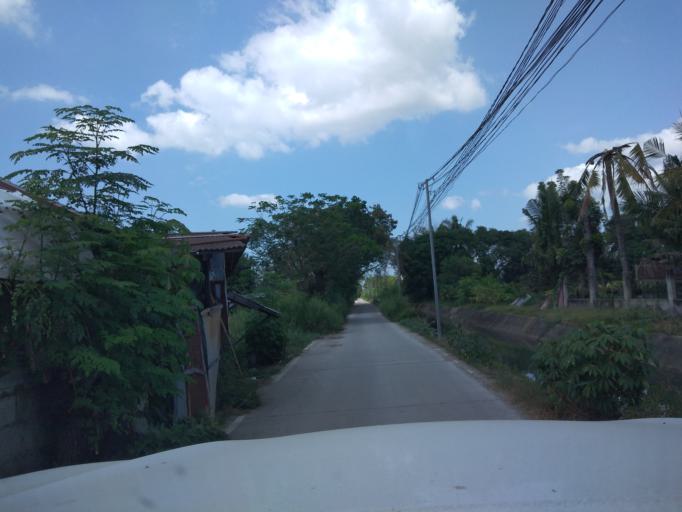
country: PH
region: Central Luzon
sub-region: Province of Pampanga
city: Bahay Pare
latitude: 15.0382
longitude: 120.8727
